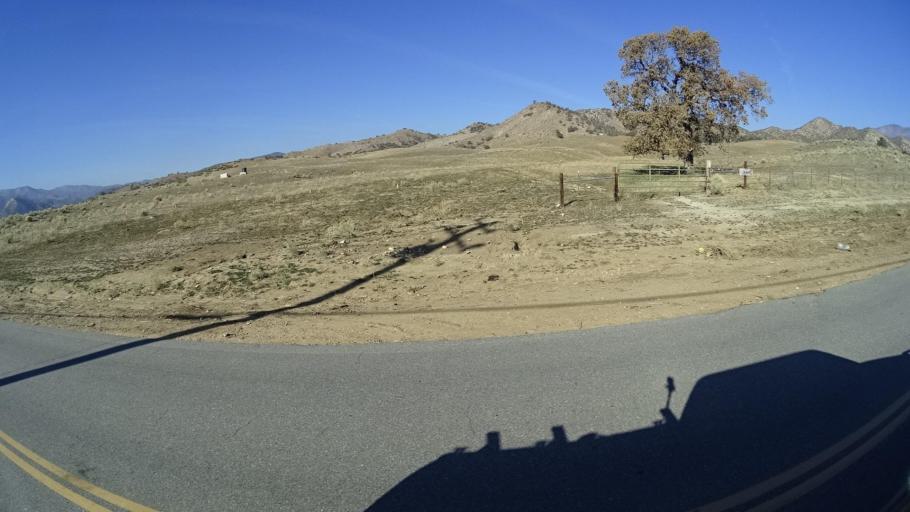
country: US
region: California
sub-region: Kern County
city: Tehachapi
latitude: 35.3197
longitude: -118.3914
